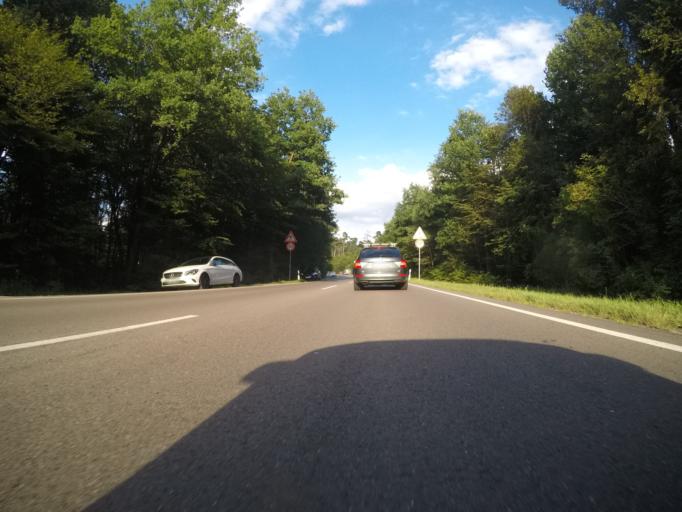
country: DE
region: Baden-Wuerttemberg
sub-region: Regierungsbezirk Stuttgart
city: Gerlingen
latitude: 48.7554
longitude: 9.1094
